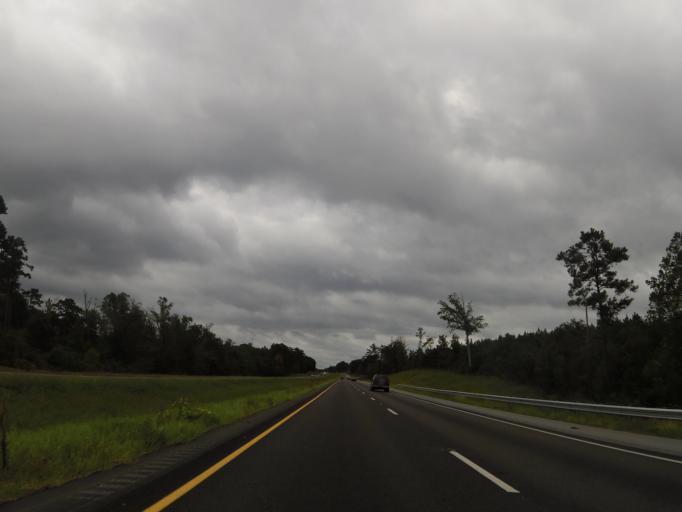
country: US
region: Alabama
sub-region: Conecuh County
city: Evergreen
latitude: 31.3506
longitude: -87.0832
